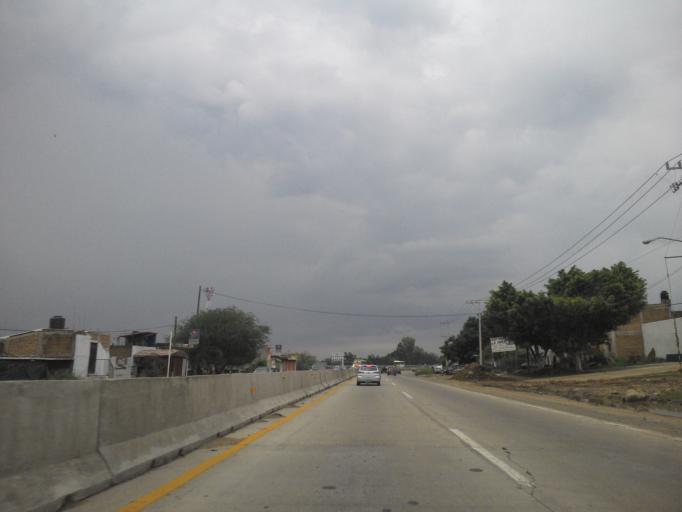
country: MX
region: Jalisco
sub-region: Tonala
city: Colonia Guadalupana
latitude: 20.5707
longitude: -103.2114
